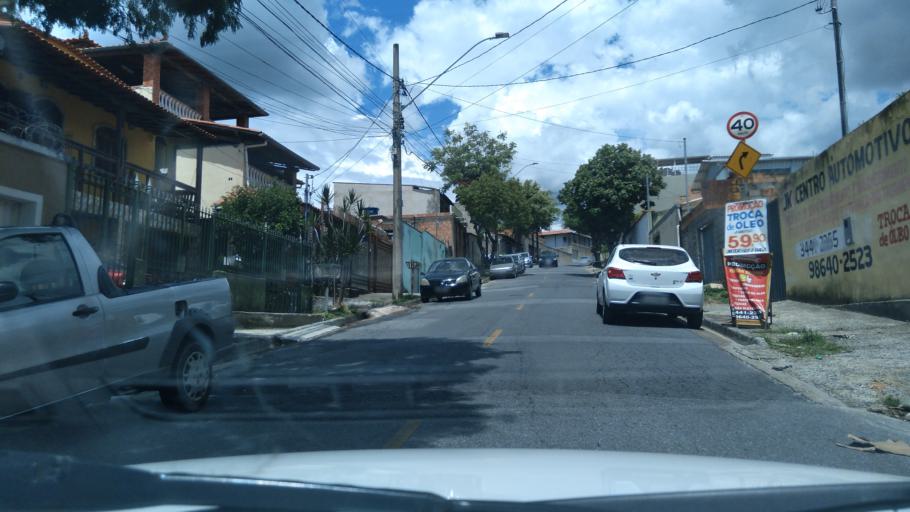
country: BR
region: Minas Gerais
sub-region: Belo Horizonte
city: Belo Horizonte
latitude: -19.8620
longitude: -43.8841
